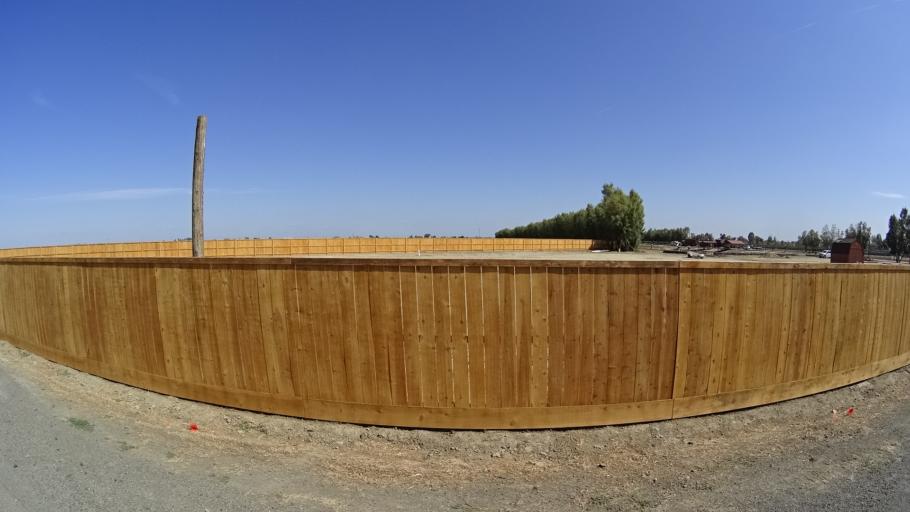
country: US
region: California
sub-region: Kings County
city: Lemoore
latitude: 36.2547
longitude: -119.7924
